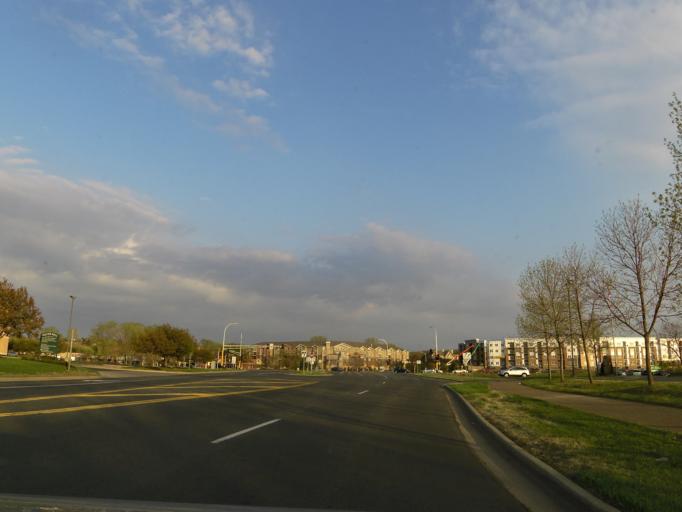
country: US
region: Minnesota
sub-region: Dakota County
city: Eagan
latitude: 44.8209
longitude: -93.2103
